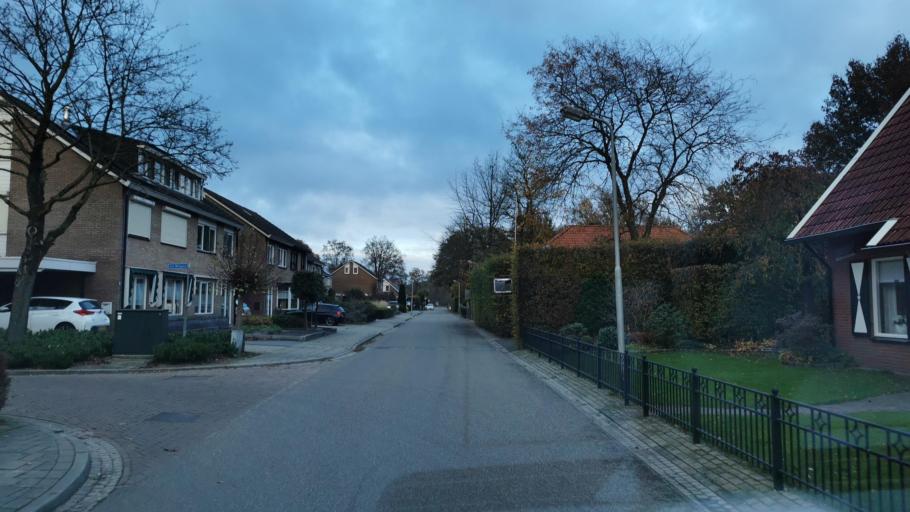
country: DE
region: North Rhine-Westphalia
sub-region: Regierungsbezirk Munster
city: Gronau
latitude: 52.2416
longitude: 7.0345
